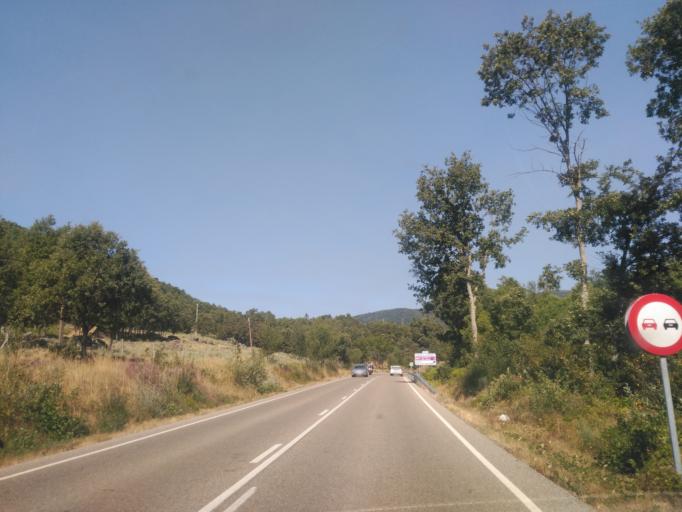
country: ES
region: Castille and Leon
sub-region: Provincia de Zamora
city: Galende
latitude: 42.1145
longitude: -6.6856
